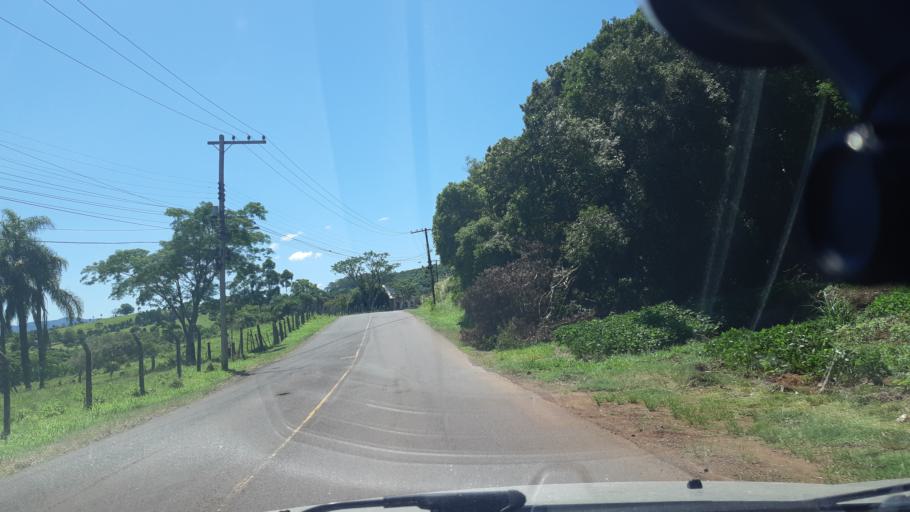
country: BR
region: Rio Grande do Sul
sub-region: Novo Hamburgo
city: Novo Hamburgo
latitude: -29.6259
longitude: -51.1020
